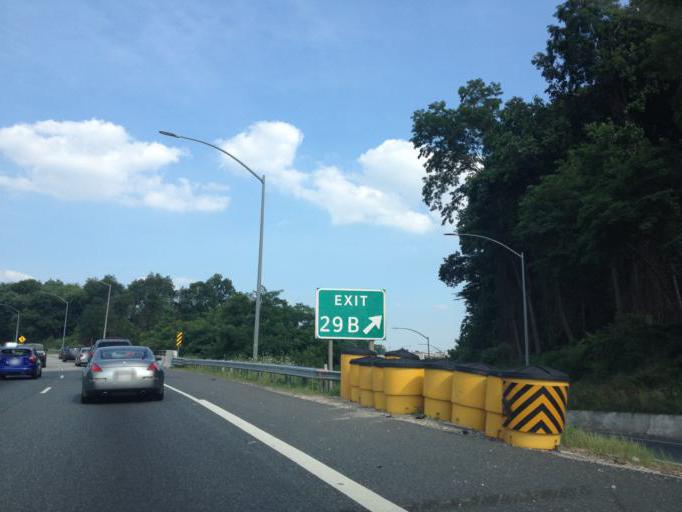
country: US
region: Maryland
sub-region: Baltimore County
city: Hampton
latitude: 39.4013
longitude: -76.5672
